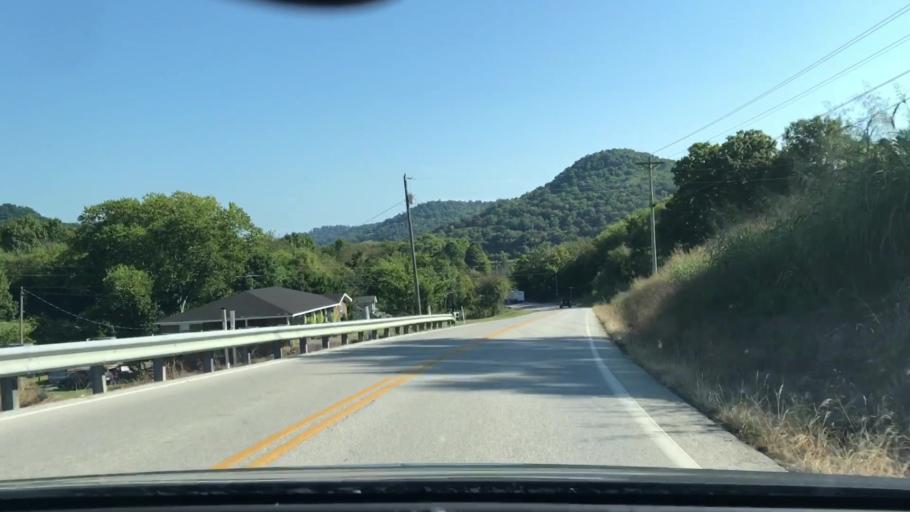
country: US
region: Tennessee
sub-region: Smith County
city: Carthage
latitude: 36.3266
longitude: -85.9072
